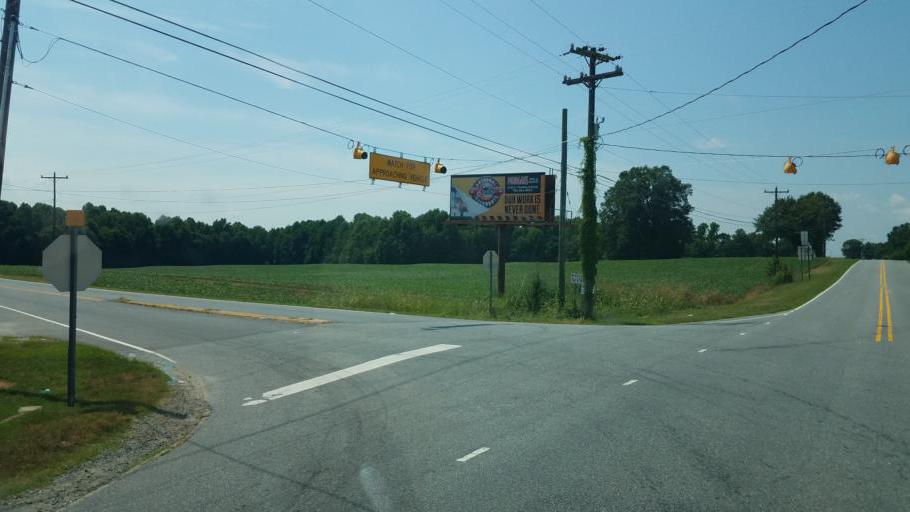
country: US
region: North Carolina
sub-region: Burke County
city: Icard
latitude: 35.5365
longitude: -81.5093
